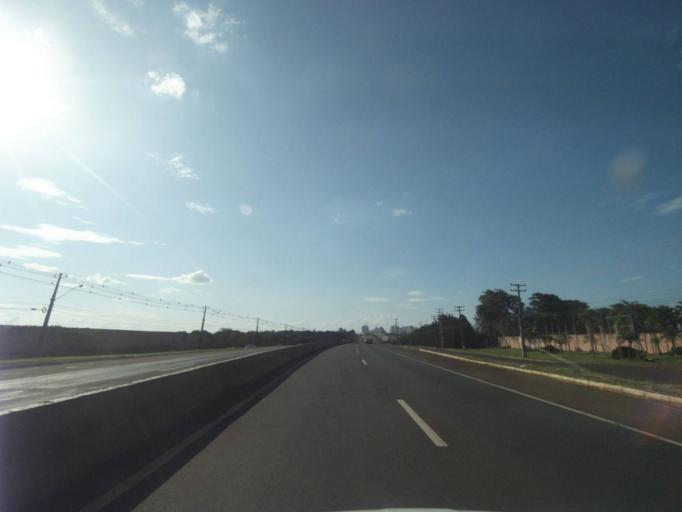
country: BR
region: Parana
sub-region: Londrina
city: Londrina
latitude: -23.3586
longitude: -51.1558
